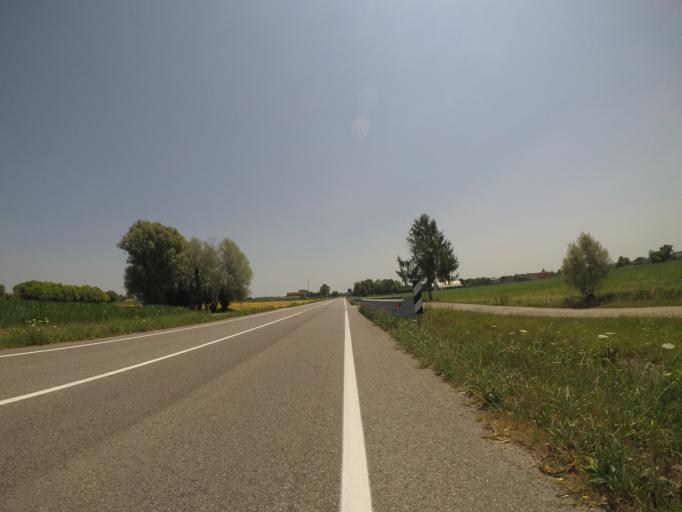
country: IT
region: Friuli Venezia Giulia
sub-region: Provincia di Udine
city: Varmo
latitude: 45.8985
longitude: 13.0075
